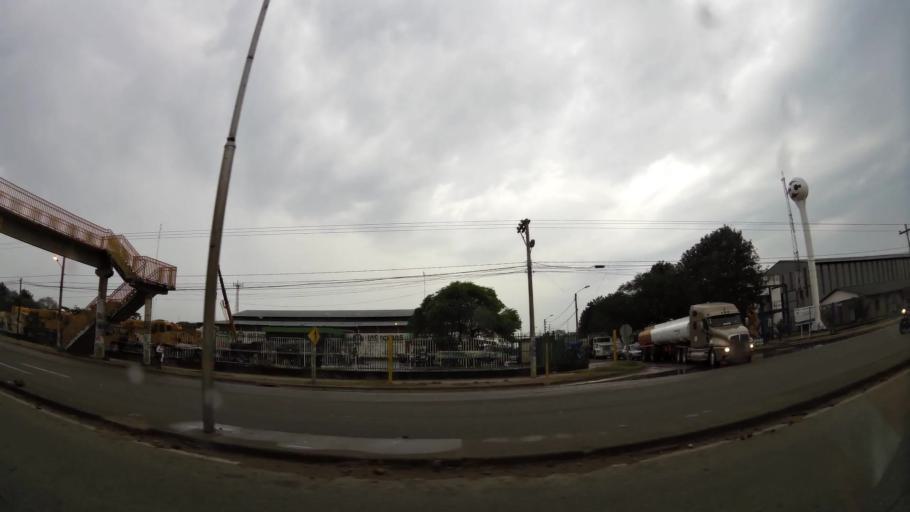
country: BO
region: Santa Cruz
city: Santa Cruz de la Sierra
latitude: -17.7746
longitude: -63.1331
